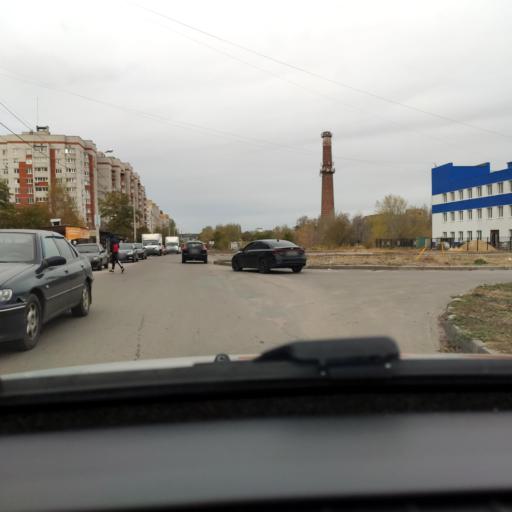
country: RU
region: Voronezj
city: Somovo
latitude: 51.6706
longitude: 39.2908
